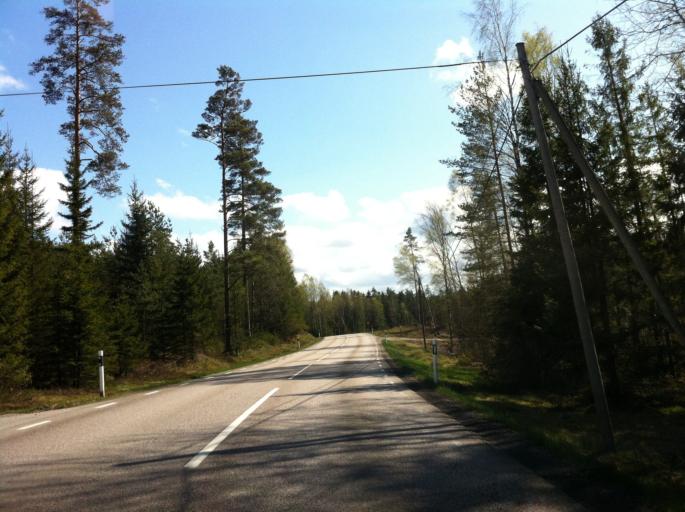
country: SE
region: Vaestra Goetaland
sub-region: Alingsas Kommun
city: Alingsas
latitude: 57.8614
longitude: 12.6138
